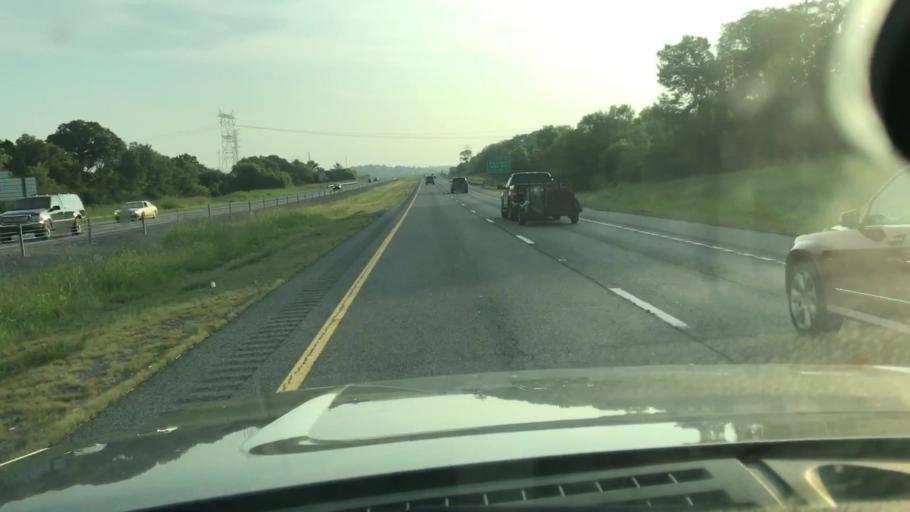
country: US
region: Tennessee
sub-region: Sumner County
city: Gallatin
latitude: 36.3654
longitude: -86.5210
